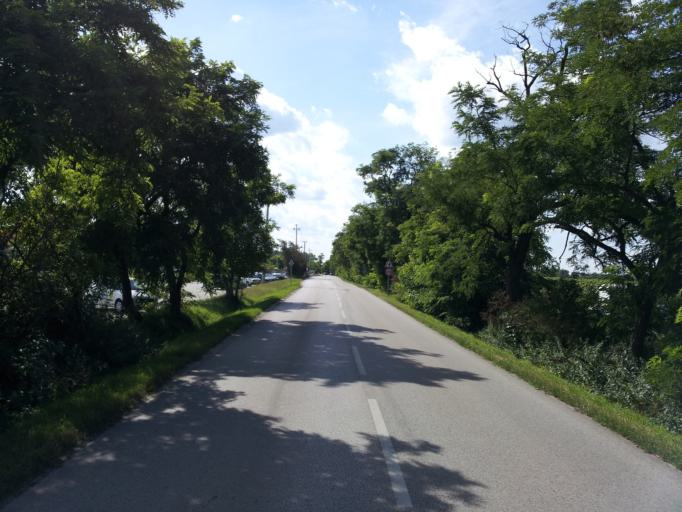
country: HU
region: Pest
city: Szigetcsep
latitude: 47.2620
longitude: 19.0124
